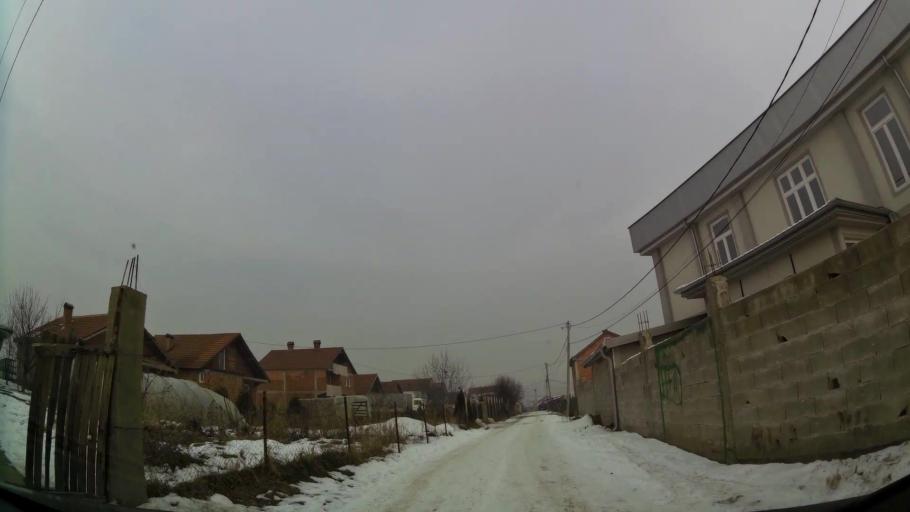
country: MK
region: Suto Orizari
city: Suto Orizare
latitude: 42.0391
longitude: 21.4156
